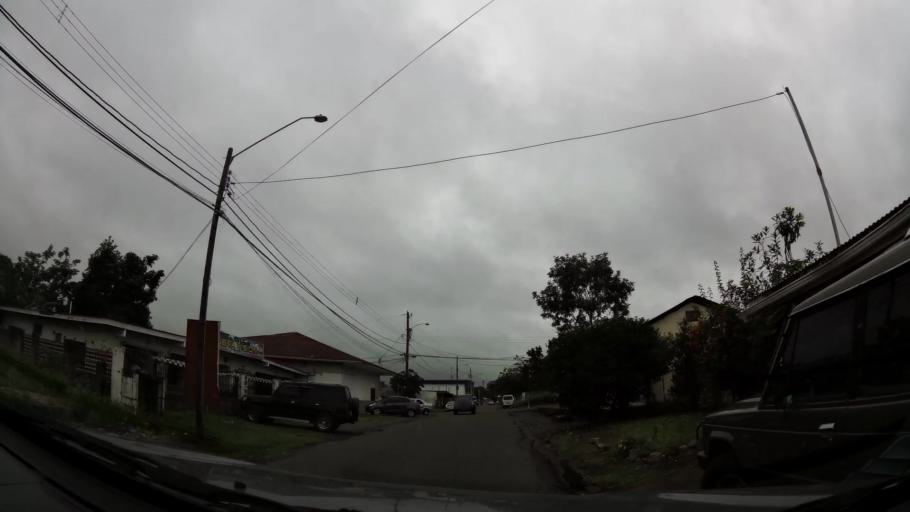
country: PA
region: Chiriqui
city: La Concepcion
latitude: 8.5189
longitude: -82.6181
